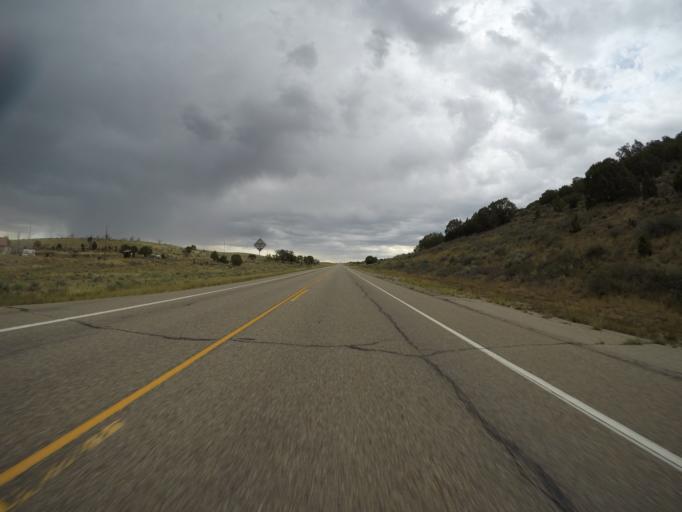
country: US
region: Colorado
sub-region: Rio Blanco County
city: Rangely
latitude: 40.3554
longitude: -108.4479
